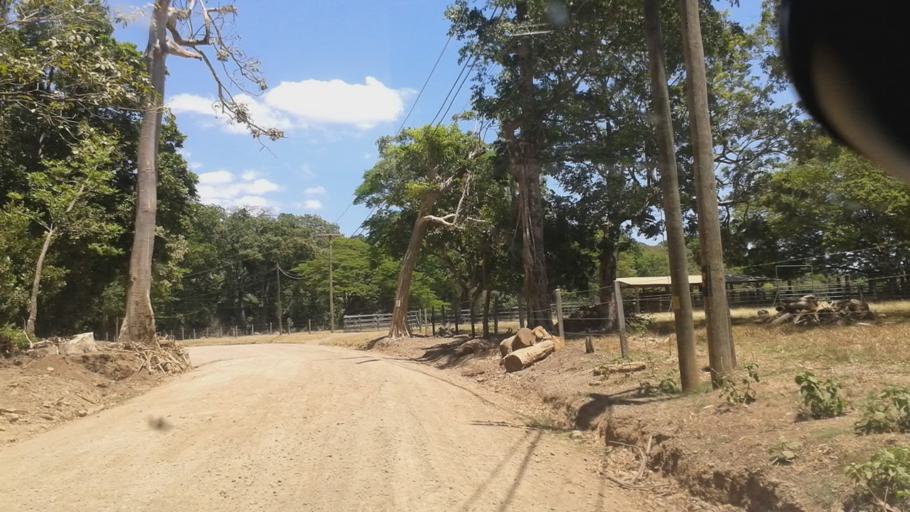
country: CR
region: Guanacaste
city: Samara
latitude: 9.9974
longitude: -85.6942
